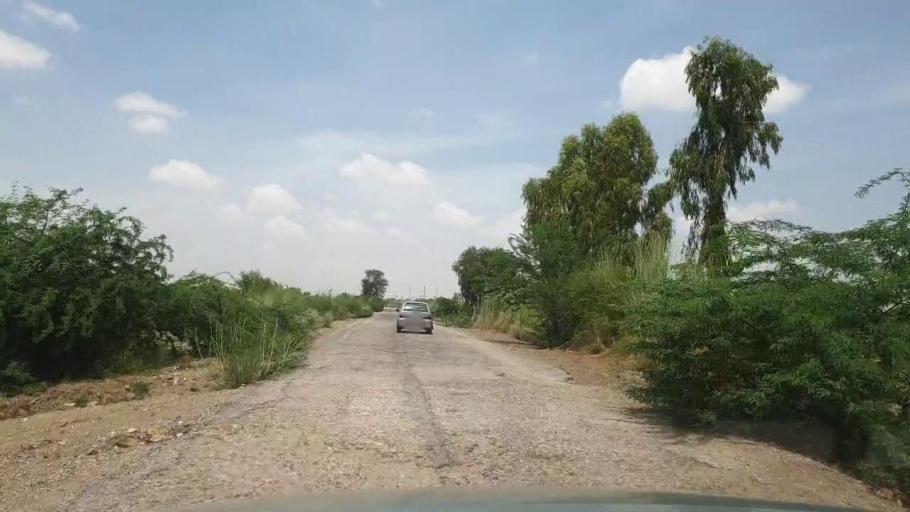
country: PK
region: Sindh
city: Kot Diji
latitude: 27.1560
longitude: 68.9732
